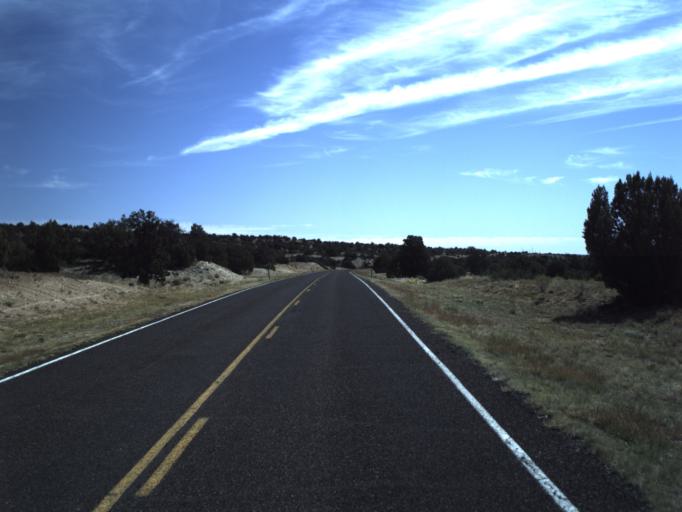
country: US
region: Utah
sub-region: Wayne County
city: Loa
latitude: 37.7388
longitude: -111.5497
